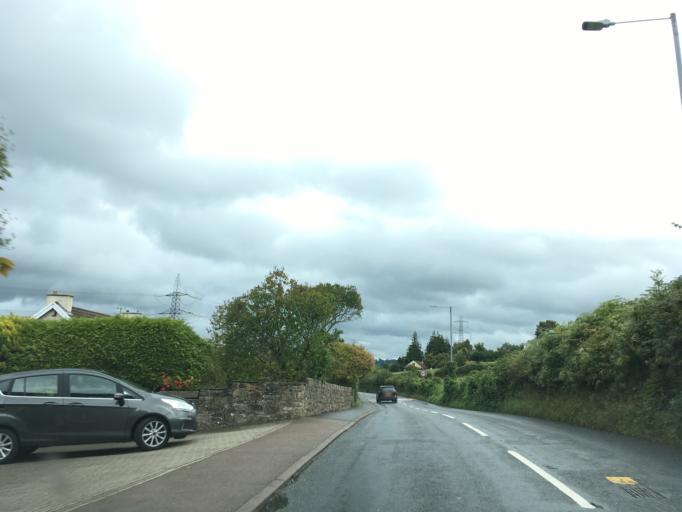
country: GB
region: Wales
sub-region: Monmouthshire
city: Gilwern
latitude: 51.8191
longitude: -3.0567
